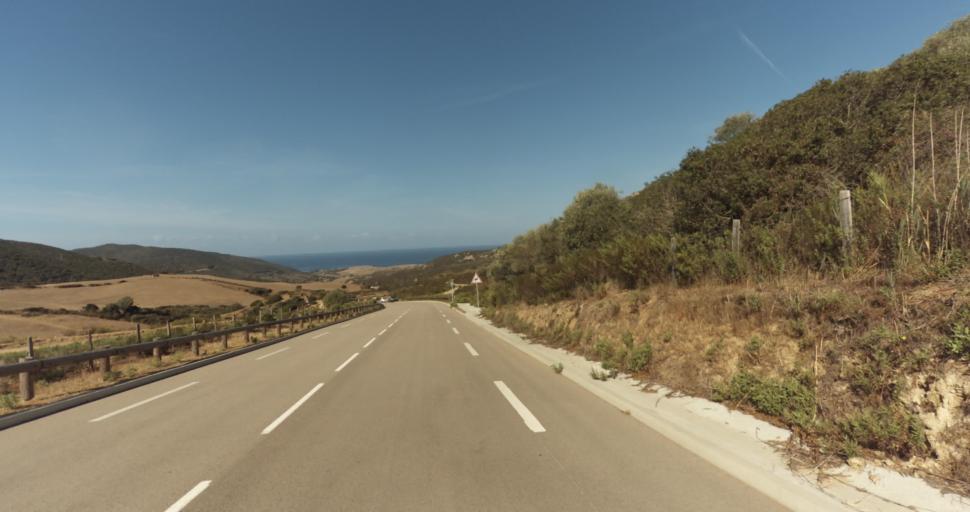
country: FR
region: Corsica
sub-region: Departement de la Corse-du-Sud
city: Ajaccio
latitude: 41.9326
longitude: 8.6746
